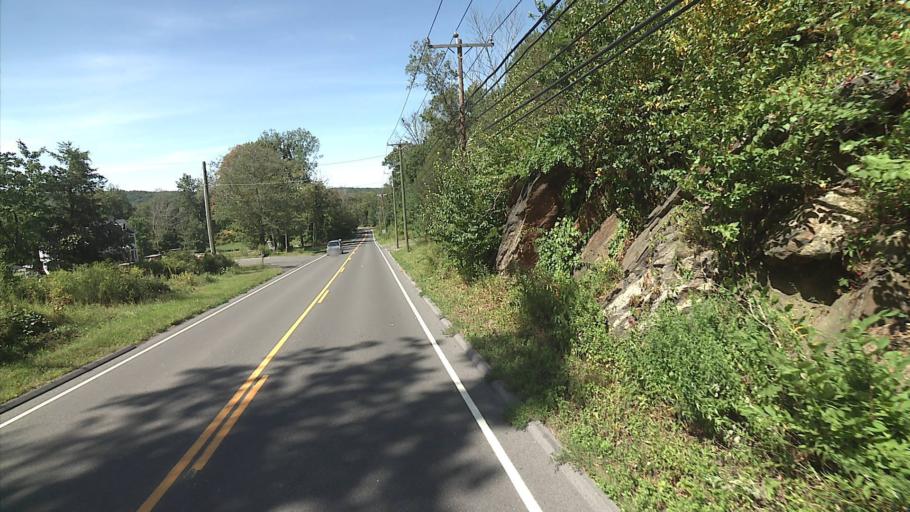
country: US
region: Connecticut
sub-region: New Haven County
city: Oxford
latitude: 41.4169
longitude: -73.1483
